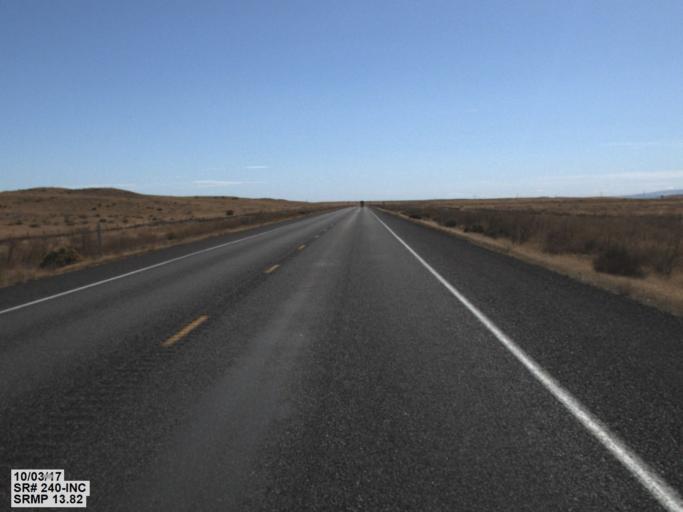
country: US
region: Washington
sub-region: Benton County
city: Benton City
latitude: 46.4545
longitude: -119.5148
